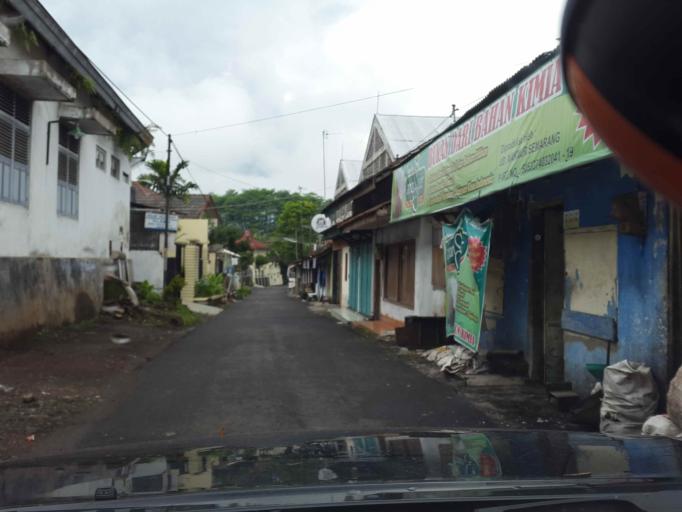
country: ID
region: Central Java
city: Salatiga
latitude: -7.3381
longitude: 110.5073
